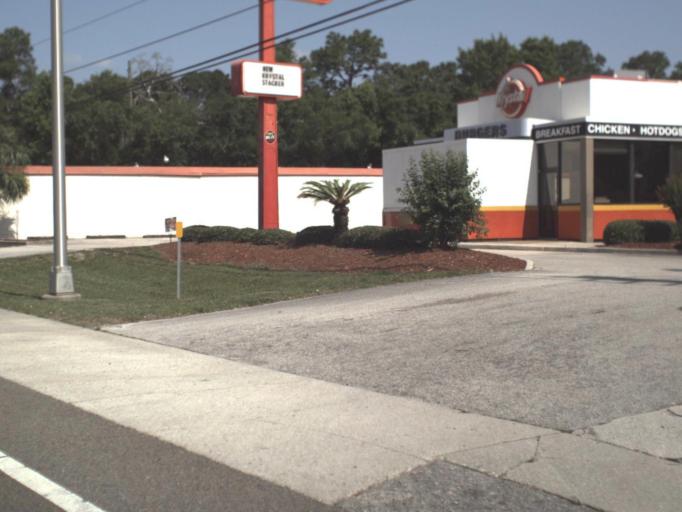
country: US
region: Florida
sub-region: Duval County
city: Jacksonville
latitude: 30.2883
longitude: -81.5752
